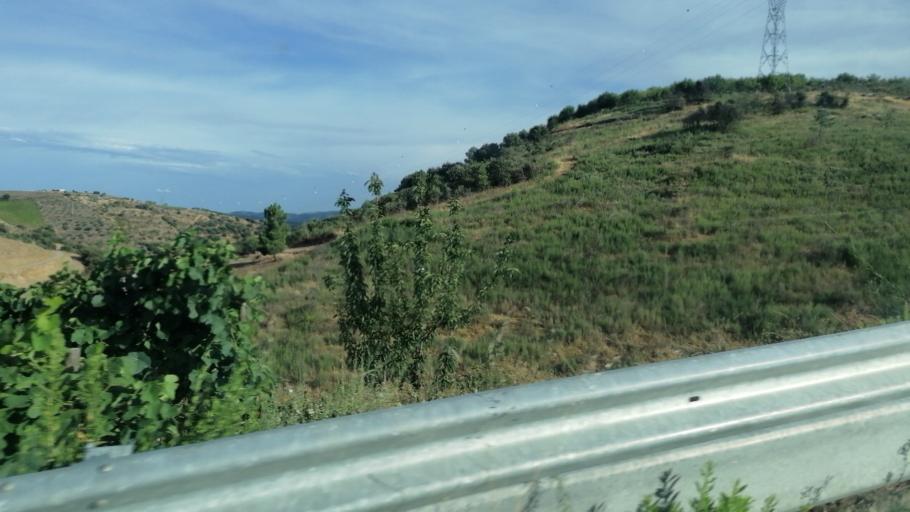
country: PT
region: Viseu
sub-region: Sao Joao da Pesqueira
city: Sao Joao da Pesqueira
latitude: 41.1412
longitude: -7.4341
